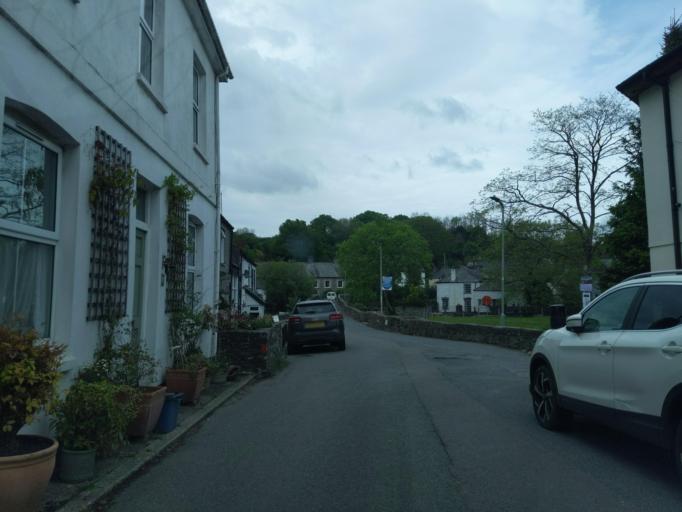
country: GB
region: England
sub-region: Devon
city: Horrabridge
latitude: 50.5096
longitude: -4.0989
